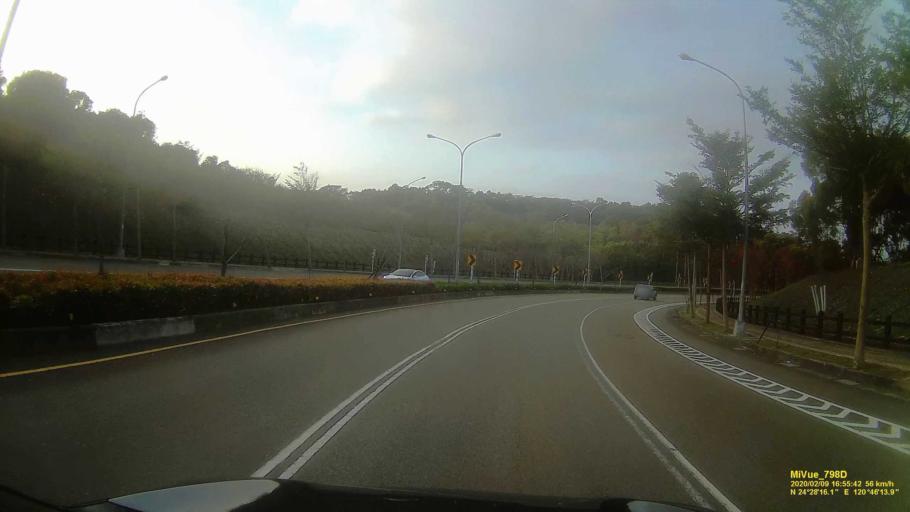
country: TW
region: Taiwan
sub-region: Miaoli
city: Miaoli
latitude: 24.4714
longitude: 120.7704
